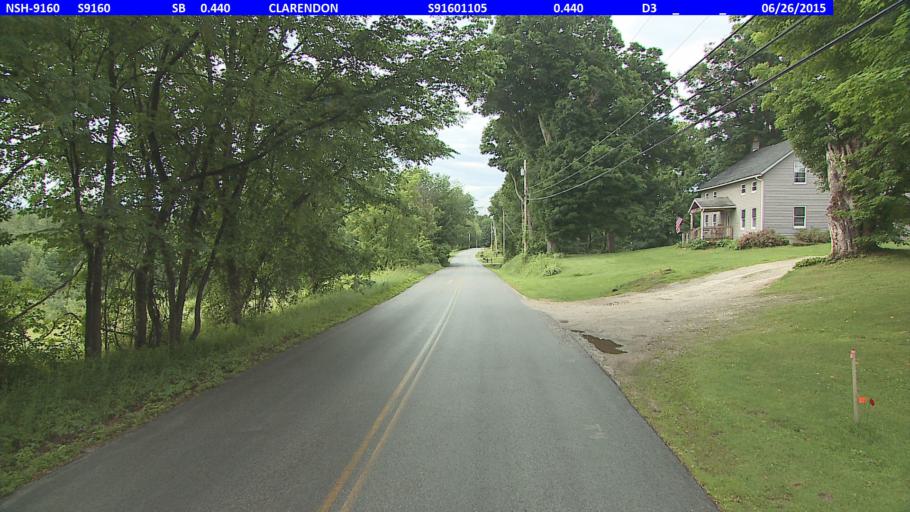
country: US
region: Vermont
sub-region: Rutland County
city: Rutland
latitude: 43.5339
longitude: -72.9461
